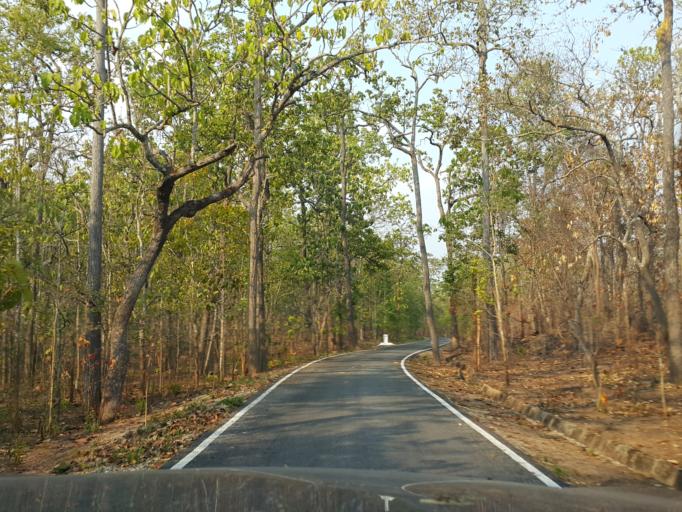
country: TH
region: Lamphun
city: Li
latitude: 17.6334
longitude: 98.8755
